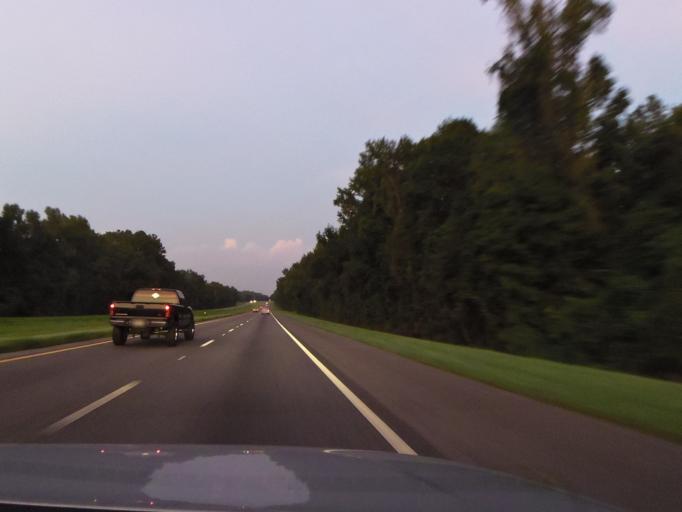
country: US
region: Florida
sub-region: Madison County
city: Madison
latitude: 30.4343
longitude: -83.5304
